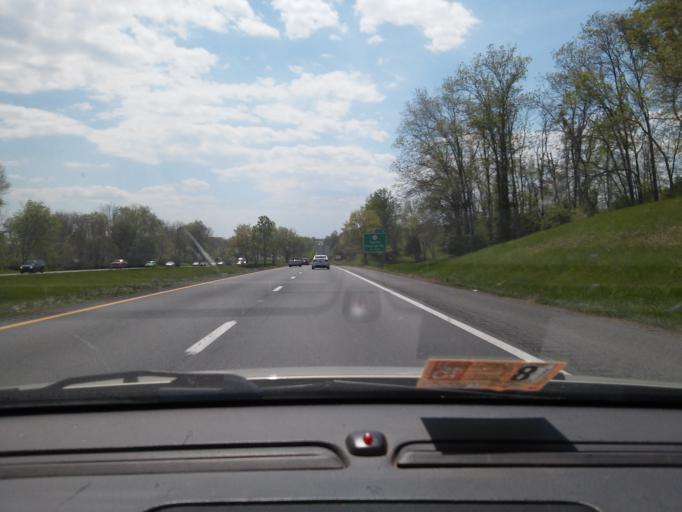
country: US
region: West Virginia
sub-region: Berkeley County
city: Martinsburg
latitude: 39.4330
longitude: -77.9949
